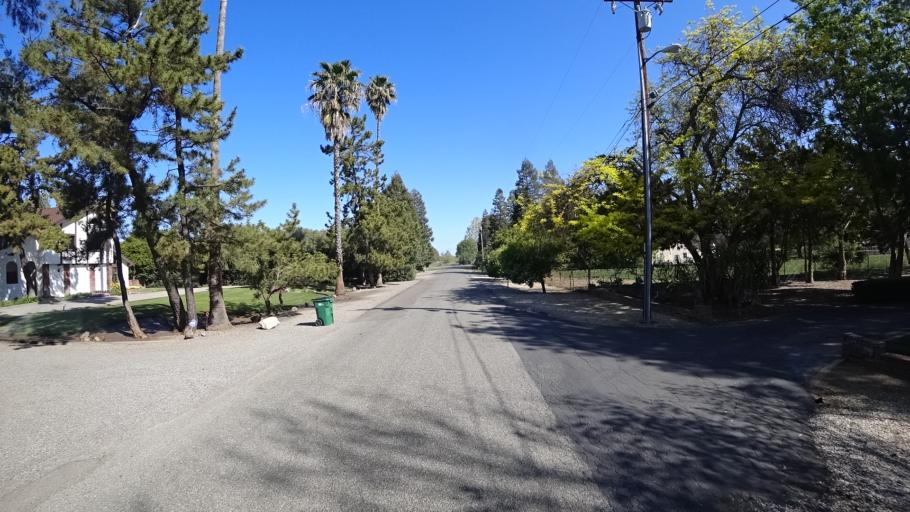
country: US
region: California
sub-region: Glenn County
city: Willows
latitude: 39.5375
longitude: -122.2028
